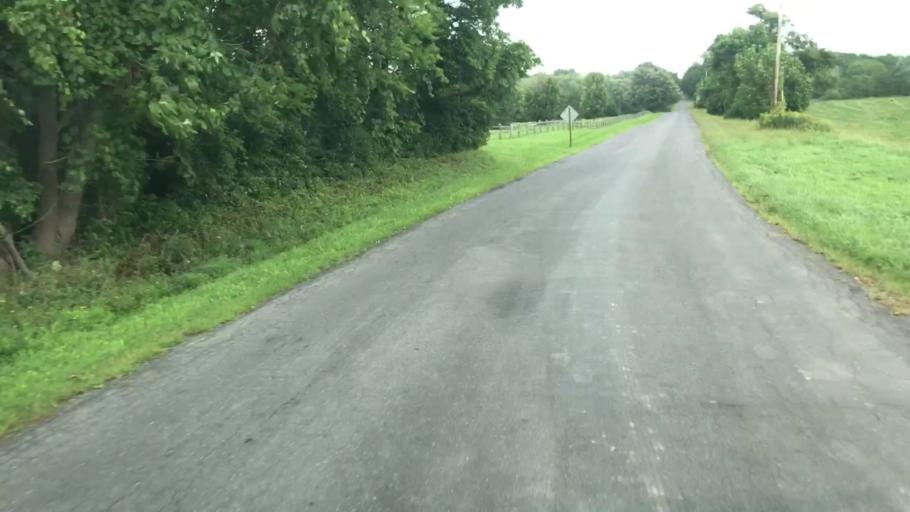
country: US
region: New York
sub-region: Onondaga County
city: Elbridge
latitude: 42.9863
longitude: -76.4614
